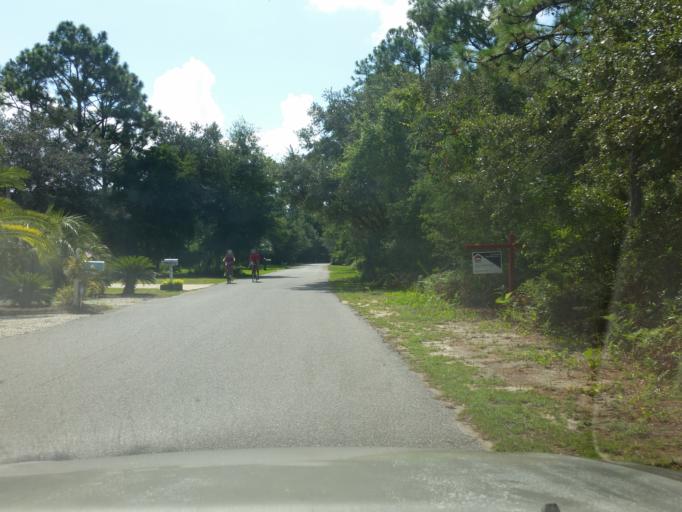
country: US
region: Alabama
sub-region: Baldwin County
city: Orange Beach
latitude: 30.3194
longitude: -87.4883
